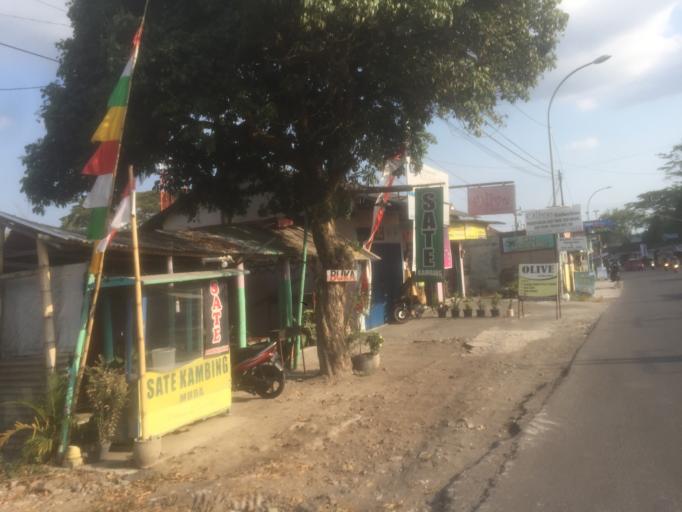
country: ID
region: Daerah Istimewa Yogyakarta
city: Sleman
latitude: -7.6836
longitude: 110.4194
